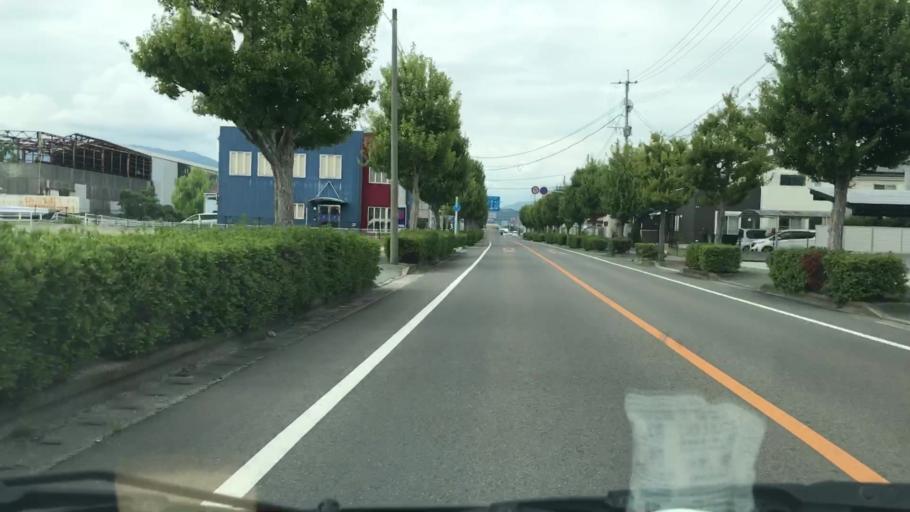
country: JP
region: Saga Prefecture
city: Saga-shi
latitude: 33.2662
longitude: 130.2622
